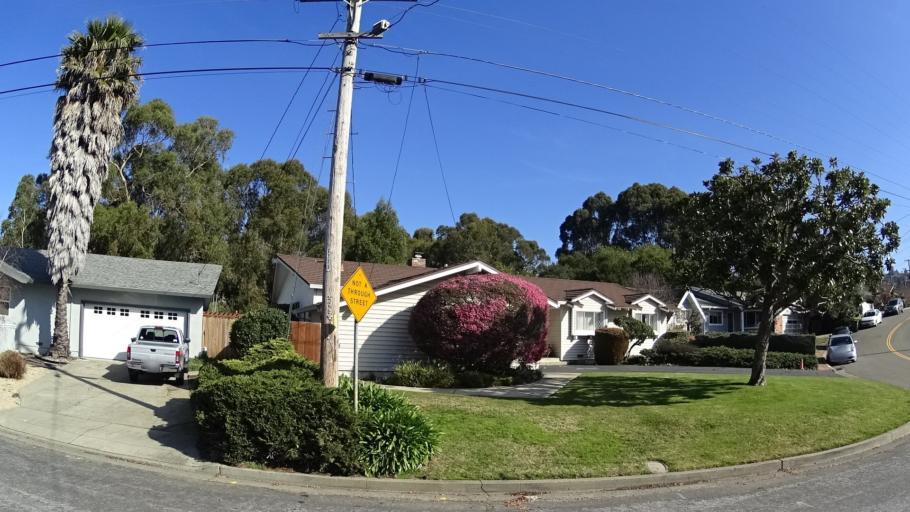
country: US
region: California
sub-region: Alameda County
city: Fairview
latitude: 37.6650
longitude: -122.0518
